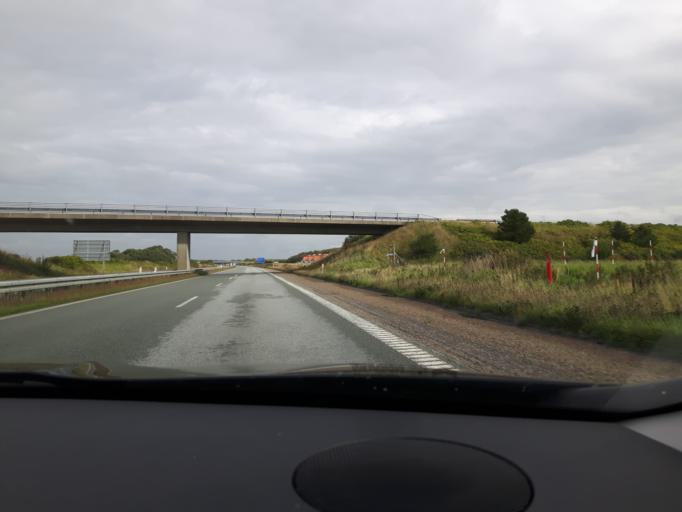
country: DK
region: North Denmark
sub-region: Hjorring Kommune
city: Hjorring
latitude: 57.4465
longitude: 10.0420
